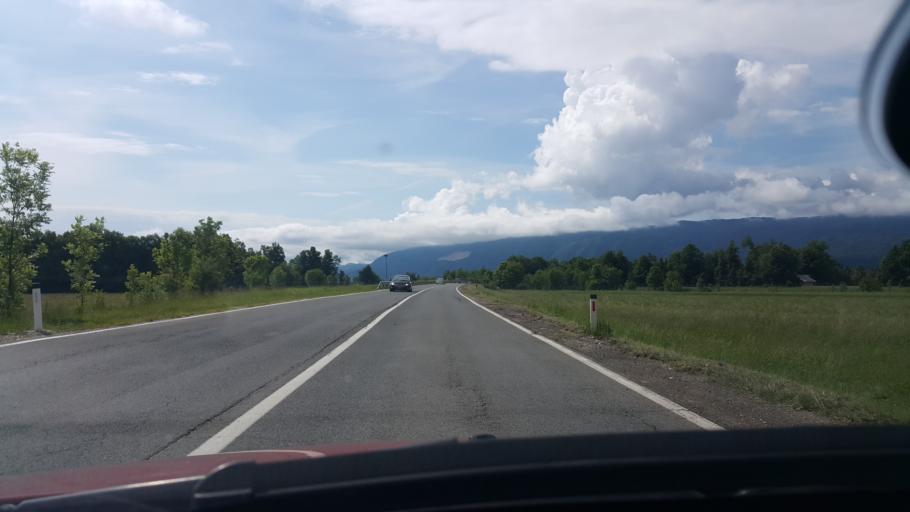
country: SI
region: Zirovnica
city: Zirovnica
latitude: 46.3828
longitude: 14.1485
